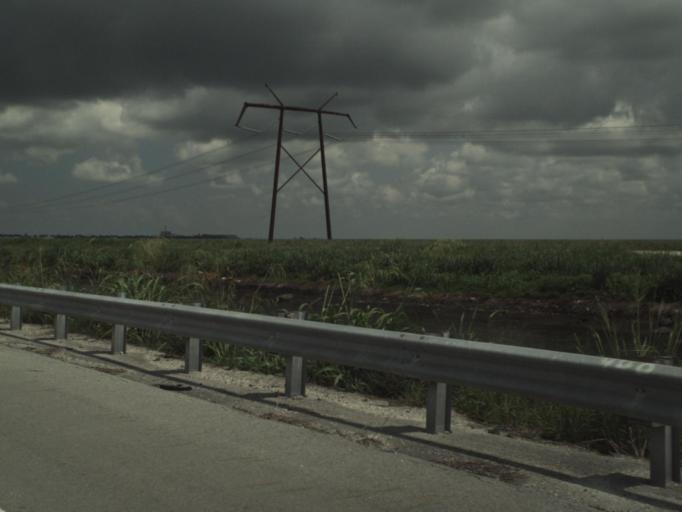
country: US
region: Florida
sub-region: Palm Beach County
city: Pahokee
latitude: 26.7894
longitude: -80.5327
